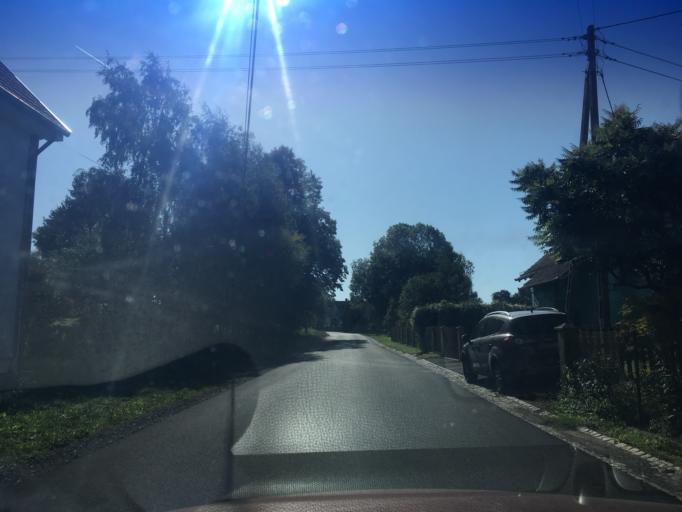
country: PL
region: Lower Silesian Voivodeship
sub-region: Powiat lubanski
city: Siekierczyn
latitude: 51.0440
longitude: 15.1687
